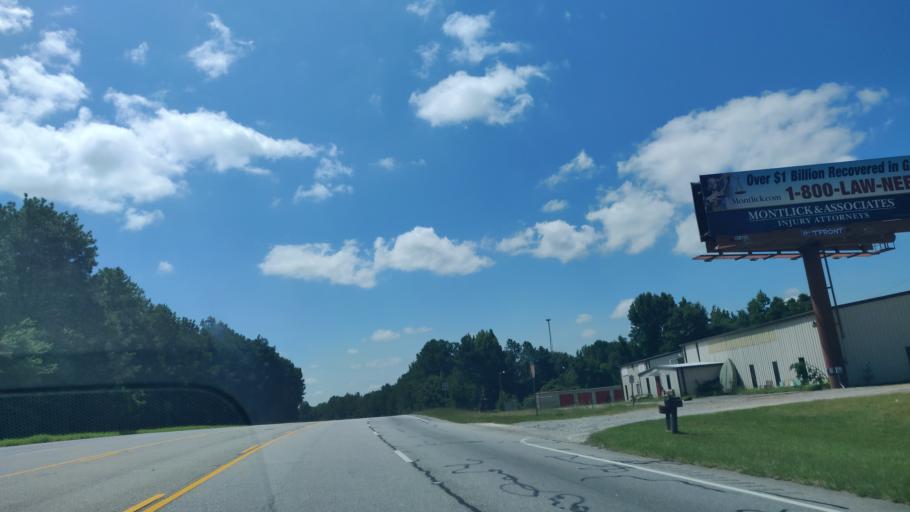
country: US
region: Georgia
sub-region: Chattahoochee County
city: Cusseta
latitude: 32.3064
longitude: -84.7908
